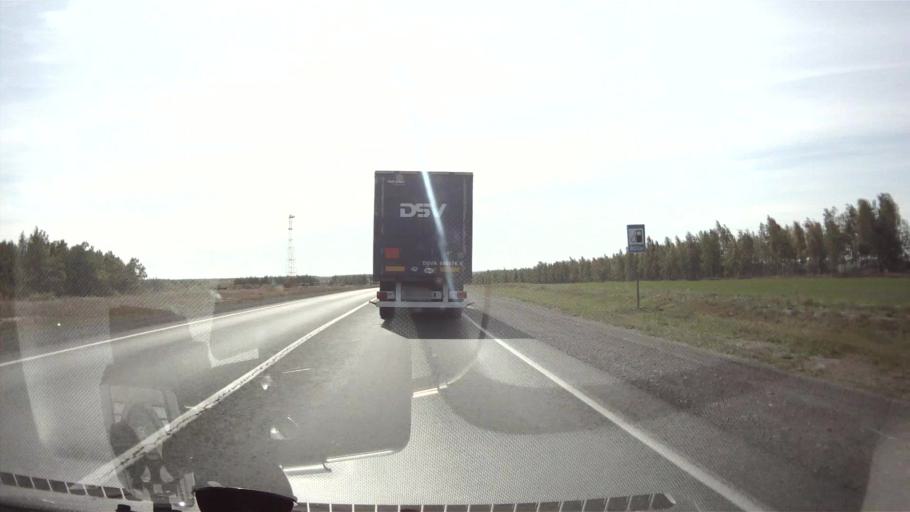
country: RU
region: Samara
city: Syzran'
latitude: 52.9317
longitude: 48.3070
